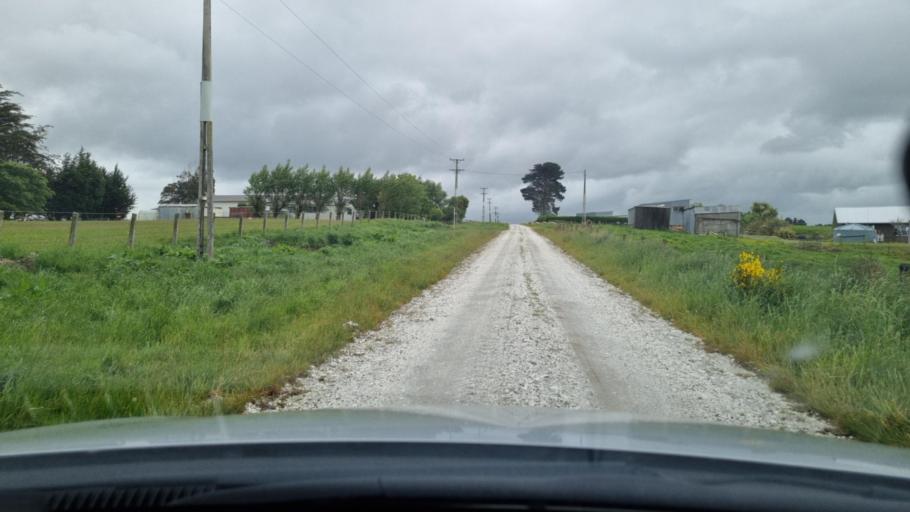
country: NZ
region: Southland
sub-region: Invercargill City
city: Invercargill
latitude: -46.4543
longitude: 168.3939
